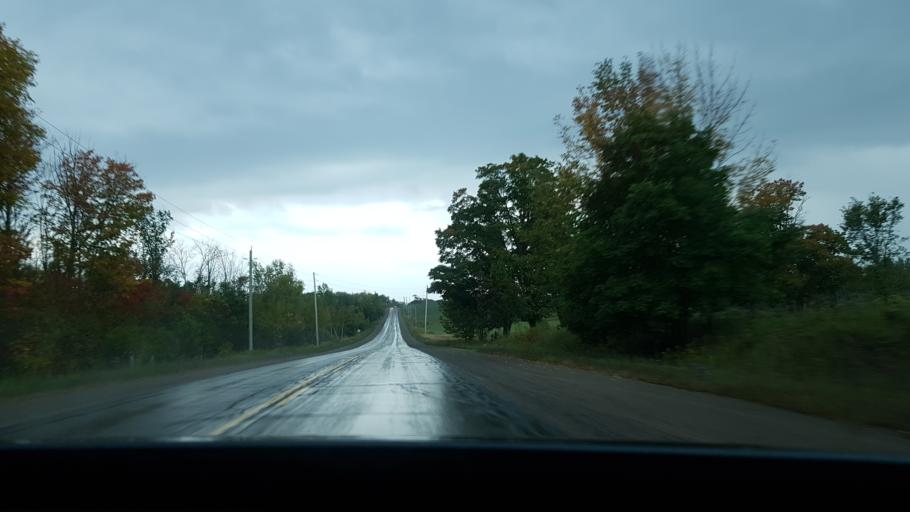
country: CA
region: Ontario
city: Omemee
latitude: 44.3700
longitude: -78.5462
